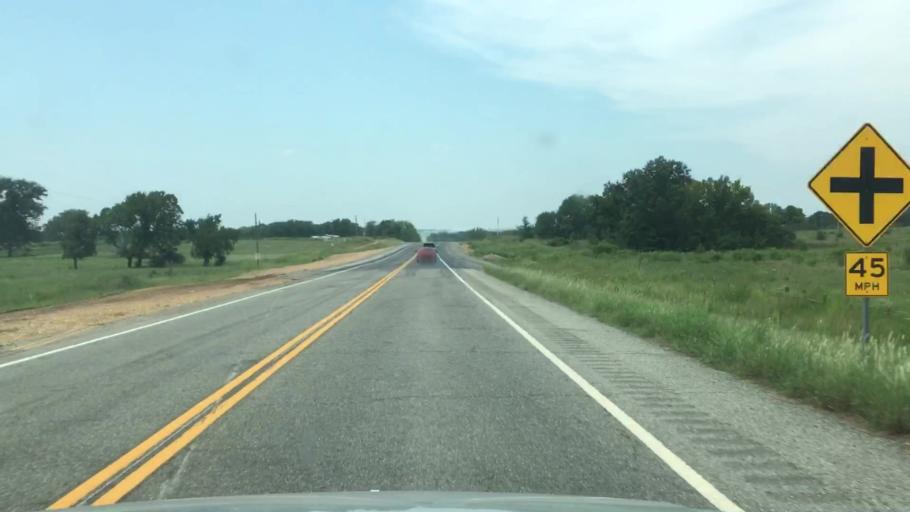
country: US
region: Oklahoma
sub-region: Muskogee County
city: Fort Gibson
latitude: 35.9369
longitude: -95.1680
